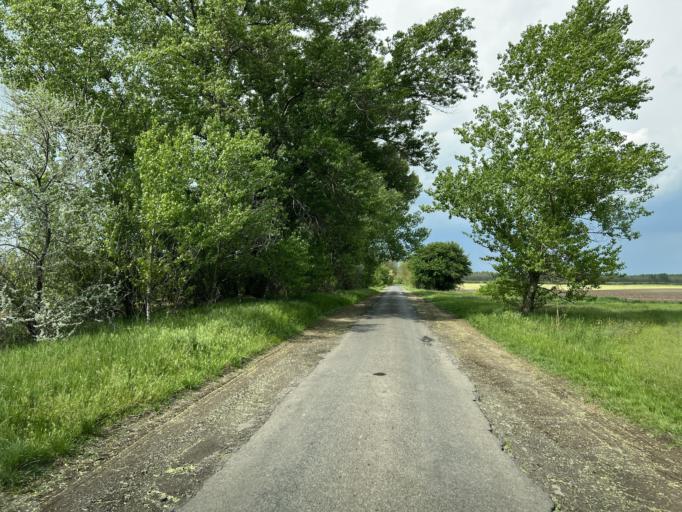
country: HU
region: Pest
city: Nagykoros
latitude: 46.9866
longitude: 19.8049
